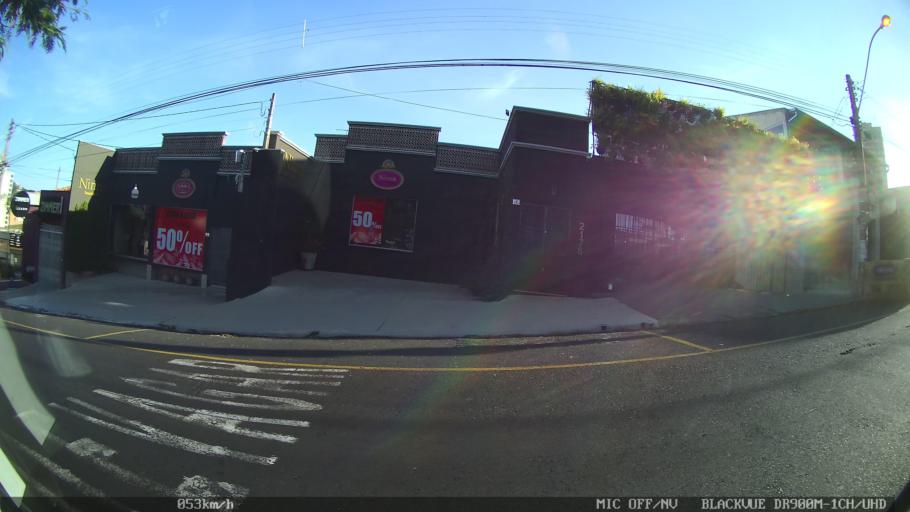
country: BR
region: Sao Paulo
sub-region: Franca
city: Franca
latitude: -20.5360
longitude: -47.3930
